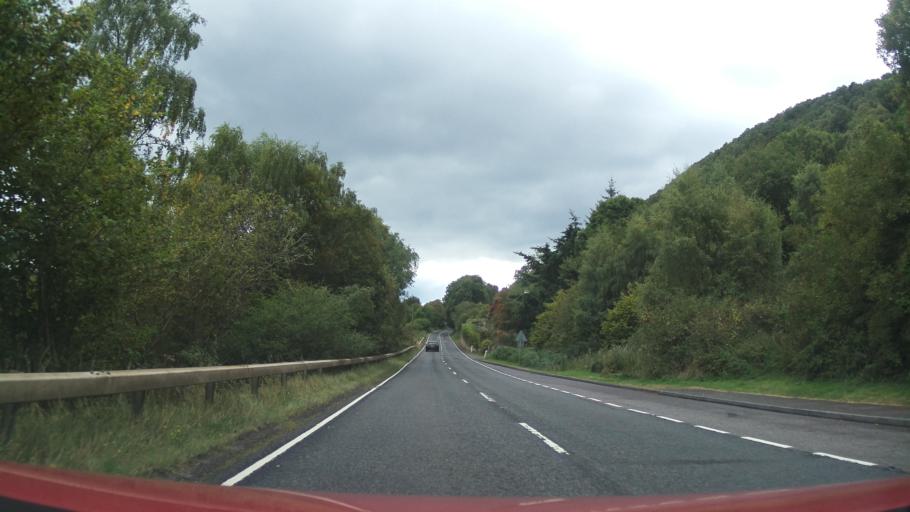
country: GB
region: Scotland
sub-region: Highland
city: Beauly
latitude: 57.3084
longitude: -4.4628
